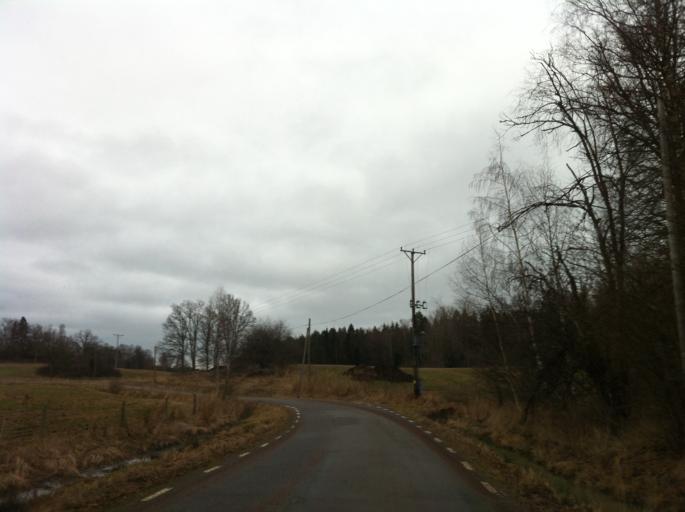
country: SE
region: Kalmar
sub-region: Vasterviks Kommun
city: Vaestervik
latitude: 57.9161
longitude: 16.6269
